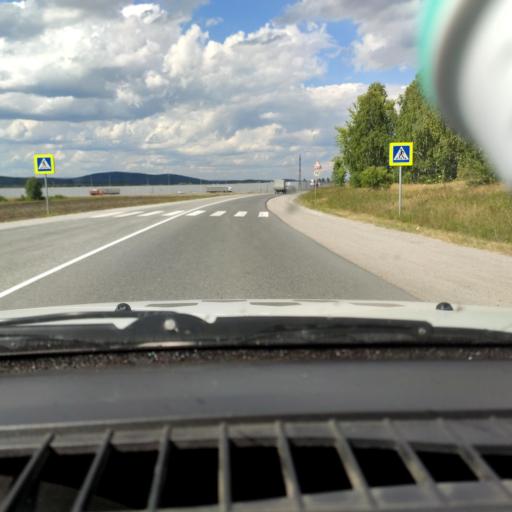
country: RU
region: Chelyabinsk
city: Miass
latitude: 54.9411
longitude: 60.0494
